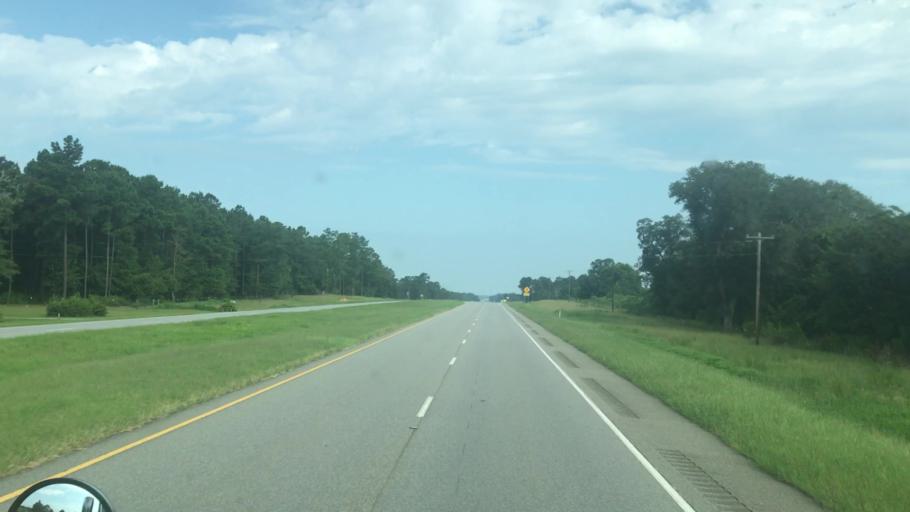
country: US
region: Georgia
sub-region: Early County
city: Blakely
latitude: 31.3182
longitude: -84.8797
